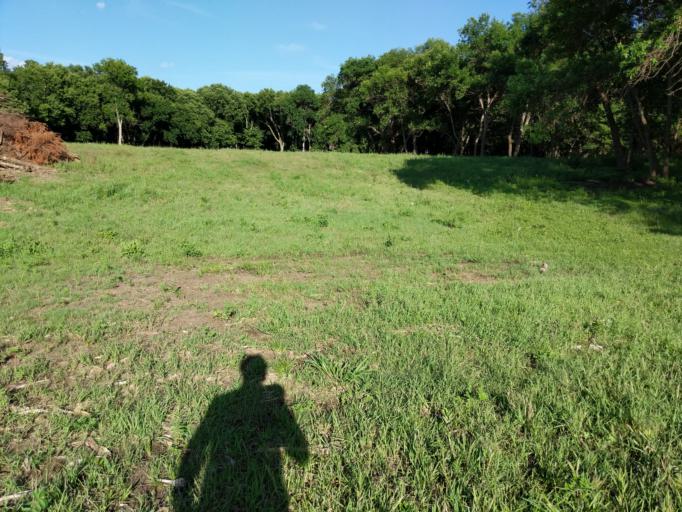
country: US
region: Kansas
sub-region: Smith County
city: Smith Center
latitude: 39.8917
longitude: -98.9487
